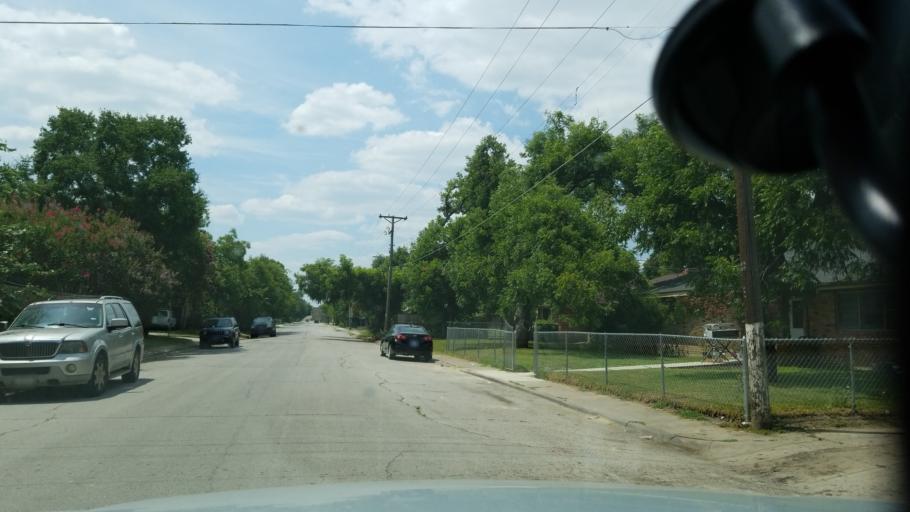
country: US
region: Texas
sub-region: Dallas County
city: Grand Prairie
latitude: 32.7543
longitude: -96.9861
